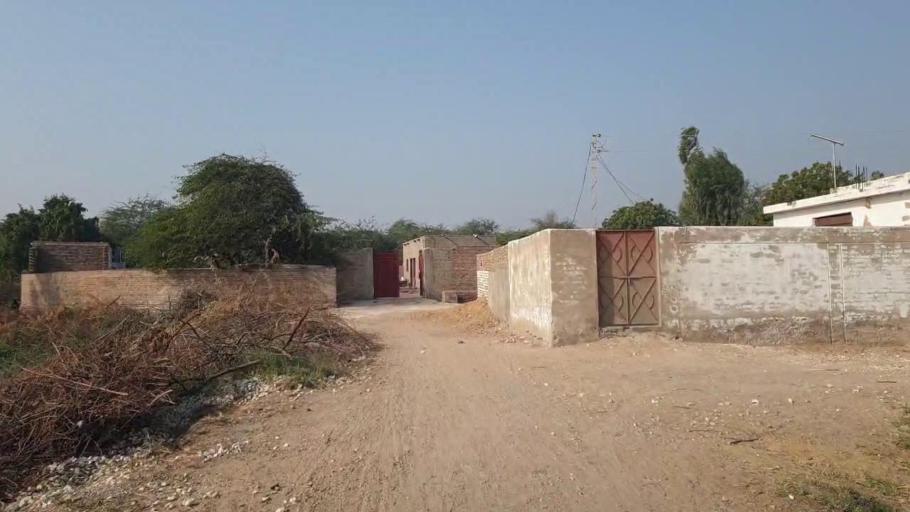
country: PK
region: Sindh
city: Kotri
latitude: 25.3312
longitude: 68.3242
